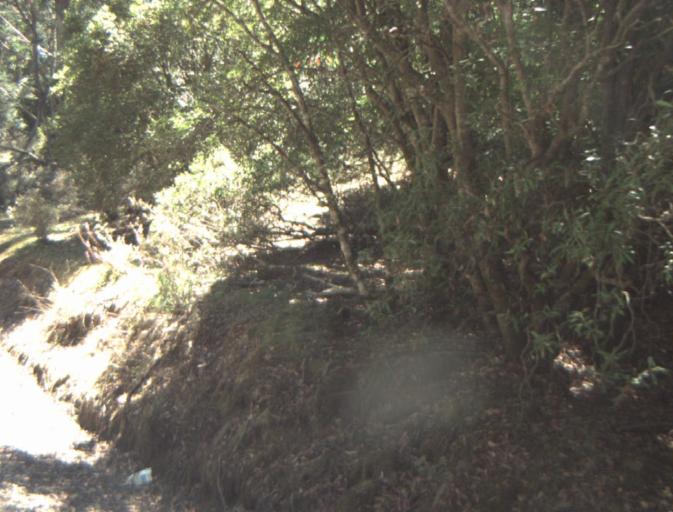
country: AU
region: Tasmania
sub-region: Dorset
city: Scottsdale
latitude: -41.3576
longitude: 147.4263
